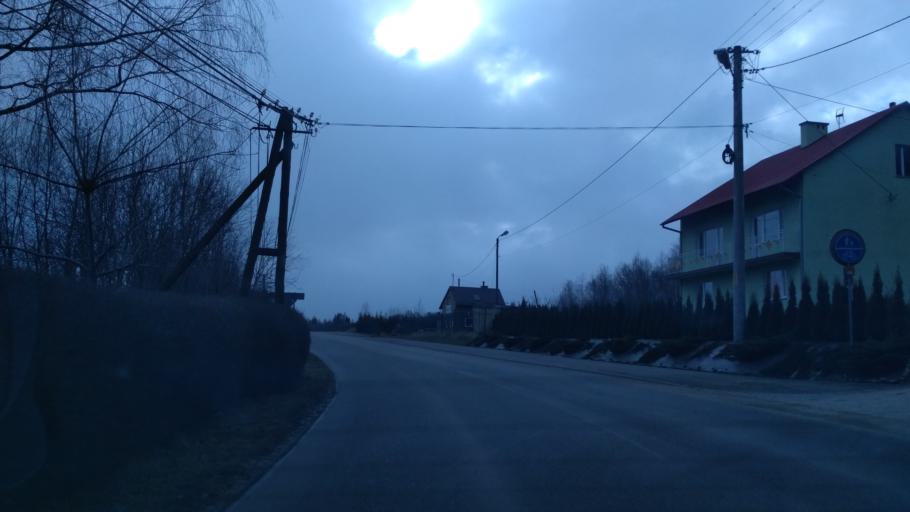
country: PL
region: Subcarpathian Voivodeship
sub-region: Powiat rzeszowski
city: Blazowa
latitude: 49.8785
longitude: 22.0954
